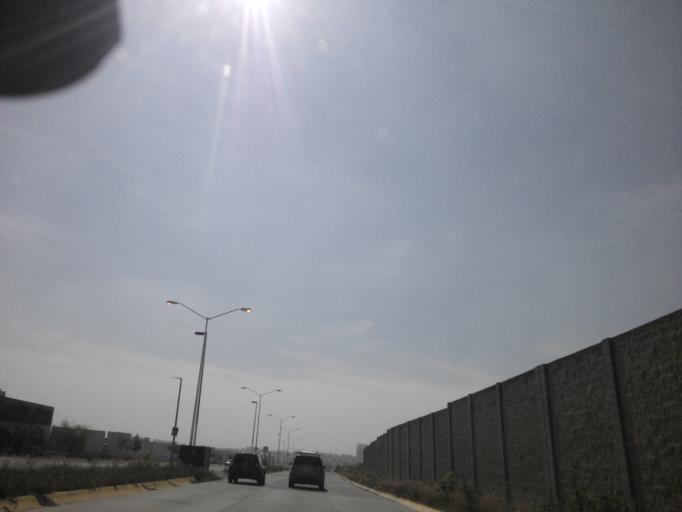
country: MX
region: Jalisco
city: Zapopan2
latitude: 20.7126
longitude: -103.4261
